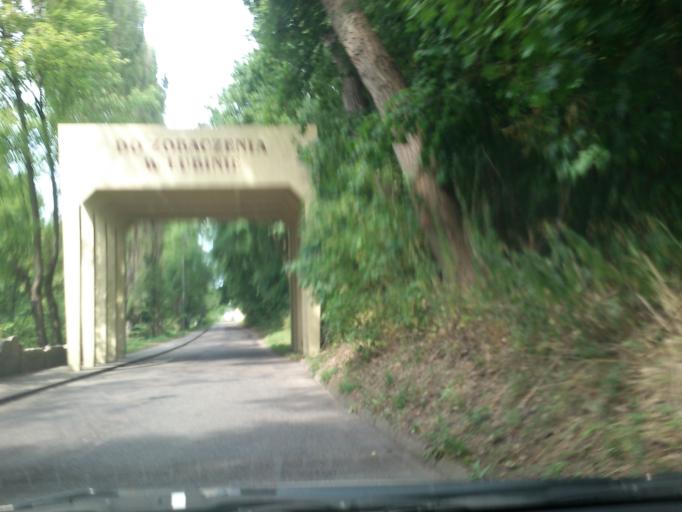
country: PL
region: West Pomeranian Voivodeship
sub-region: Powiat kamienski
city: Miedzyzdroje
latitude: 53.8753
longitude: 14.4278
